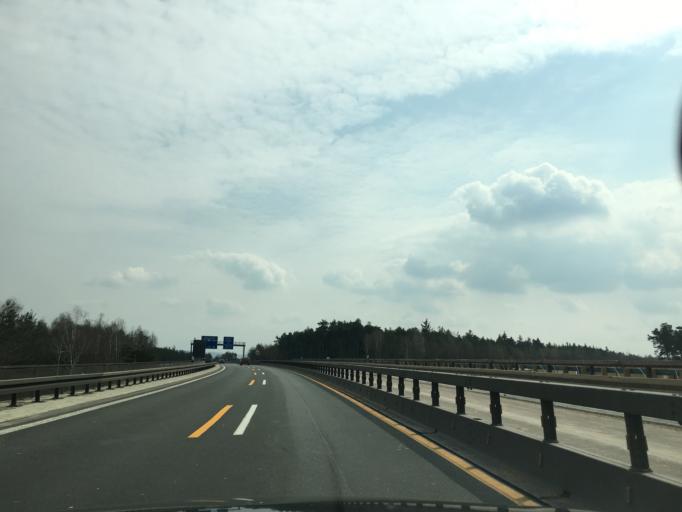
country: DE
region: Bavaria
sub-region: Regierungsbezirk Mittelfranken
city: Rothenbach an der Pegnitz
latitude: 49.4613
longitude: 11.2347
